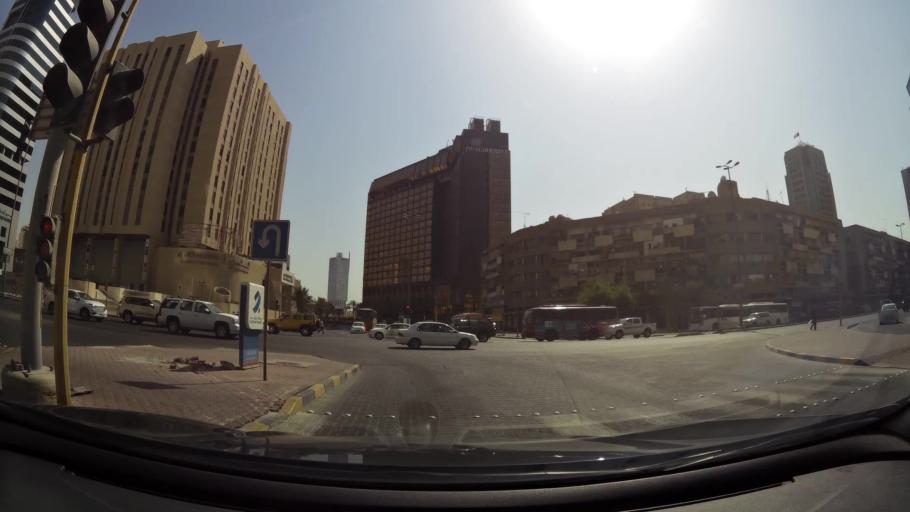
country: KW
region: Al Asimah
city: Kuwait City
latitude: 29.3660
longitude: 47.9662
